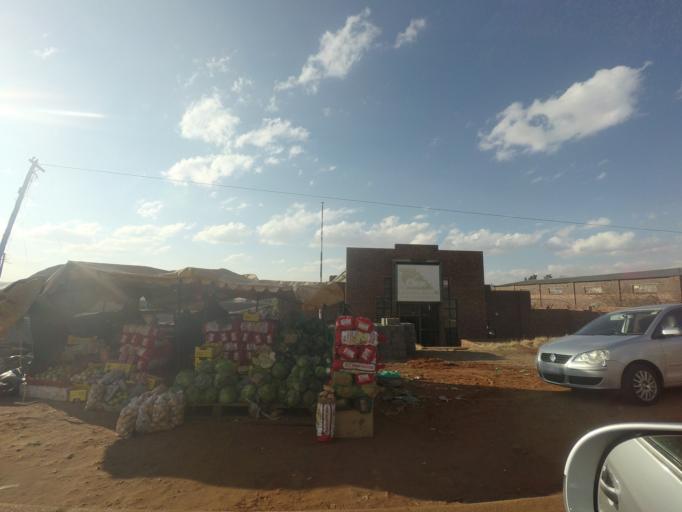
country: LS
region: Leribe
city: Maputsoe
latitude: -28.8893
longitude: 27.9088
